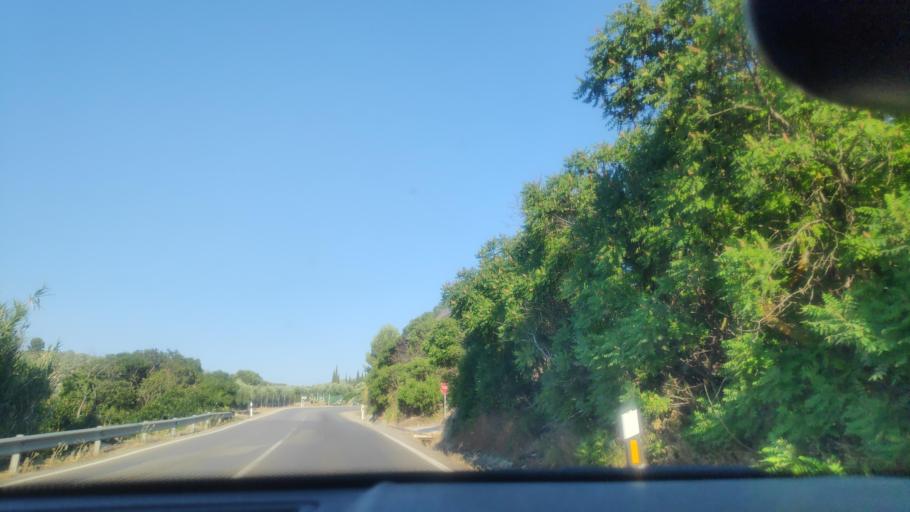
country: ES
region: Andalusia
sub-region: Provincia de Jaen
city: Jaen
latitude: 37.7481
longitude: -3.7921
